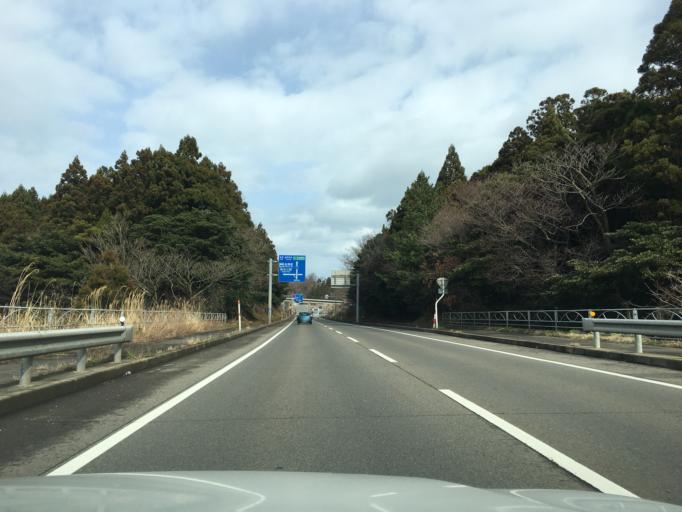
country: JP
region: Yamagata
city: Yuza
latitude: 39.2616
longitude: 139.9252
